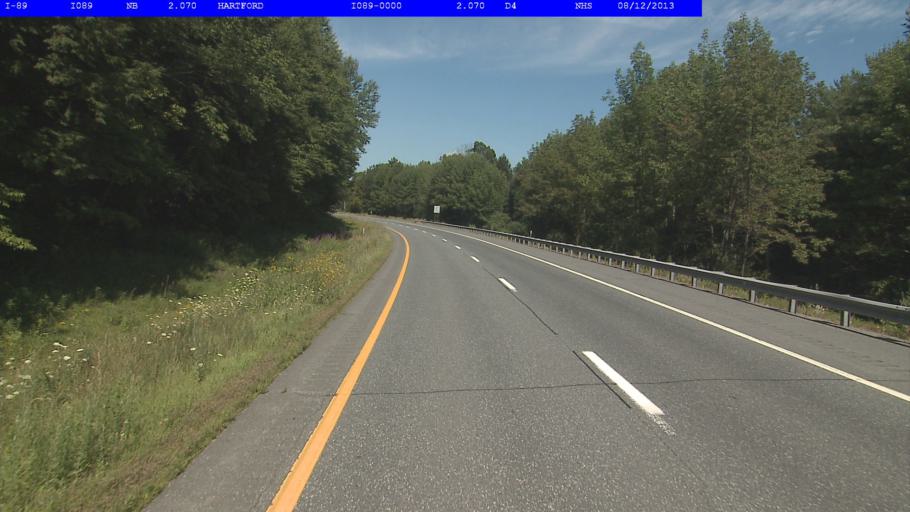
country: US
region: Vermont
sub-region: Windsor County
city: White River Junction
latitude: 43.6583
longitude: -72.3513
